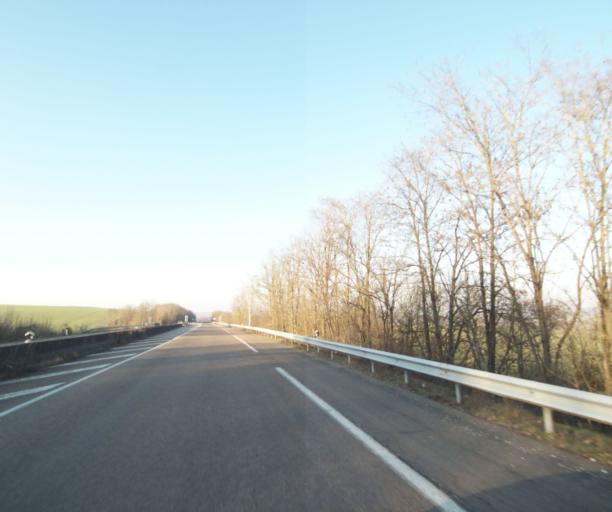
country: FR
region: Champagne-Ardenne
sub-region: Departement de la Haute-Marne
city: Chevillon
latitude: 48.5335
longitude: 5.0914
